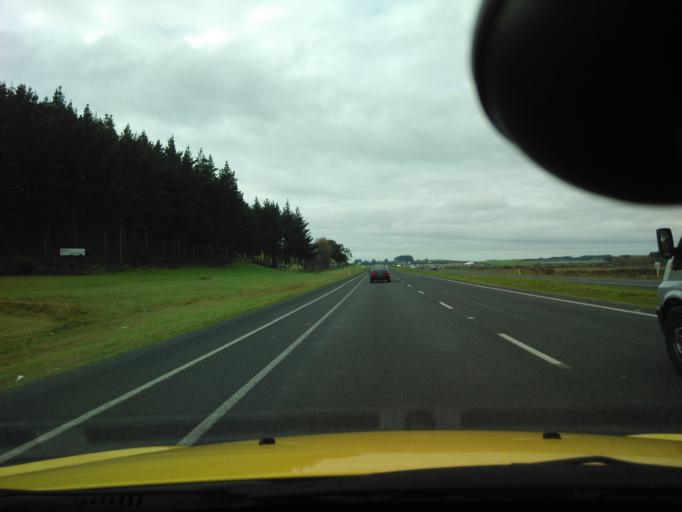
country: NZ
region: Waikato
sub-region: Waikato District
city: Te Kauwhata
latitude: -37.3420
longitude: 175.0661
